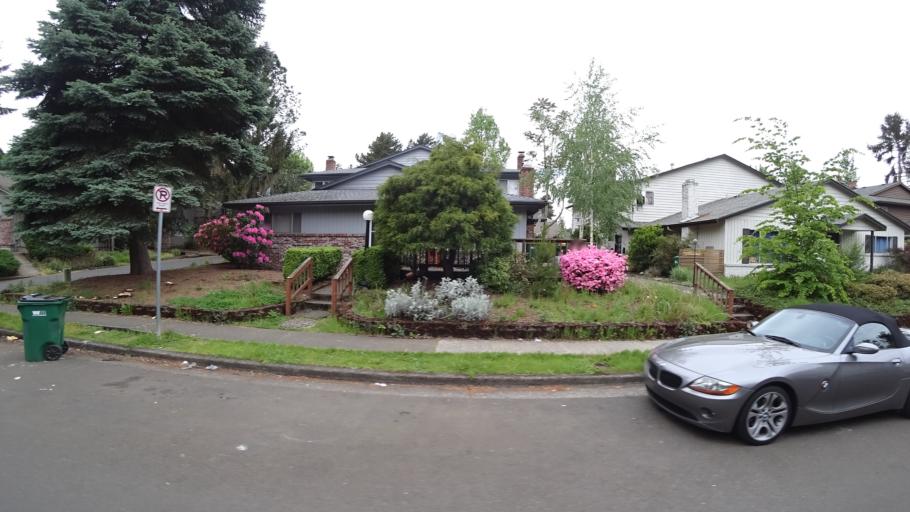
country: US
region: Oregon
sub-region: Washington County
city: Beaverton
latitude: 45.4759
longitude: -122.8148
